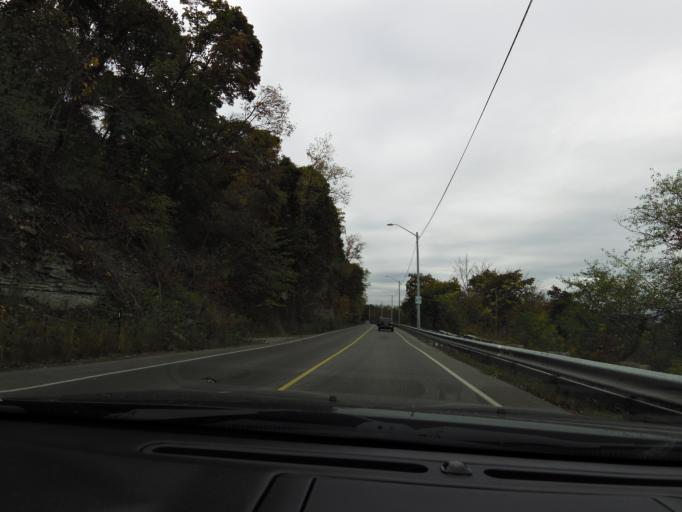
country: CA
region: Ontario
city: Hamilton
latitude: 43.2440
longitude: -79.8532
